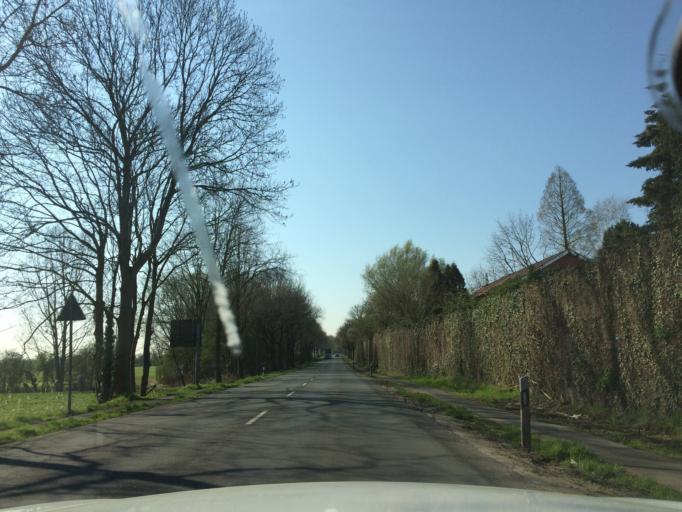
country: DE
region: North Rhine-Westphalia
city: Herten
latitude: 51.5982
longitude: 7.0950
